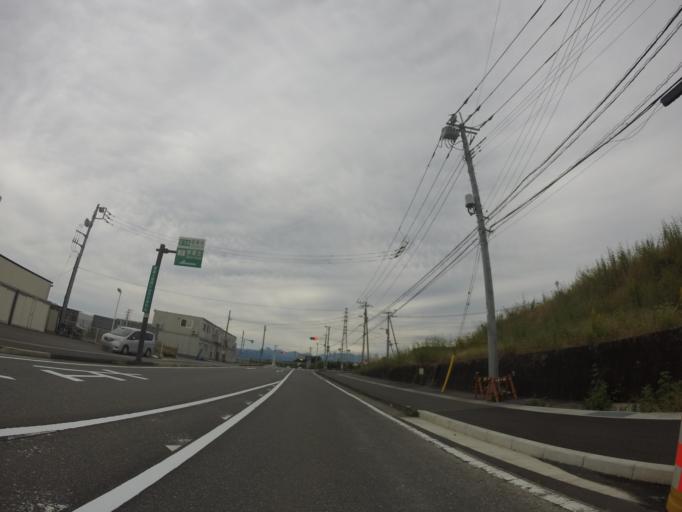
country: JP
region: Shizuoka
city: Fuji
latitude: 35.2003
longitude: 138.6737
